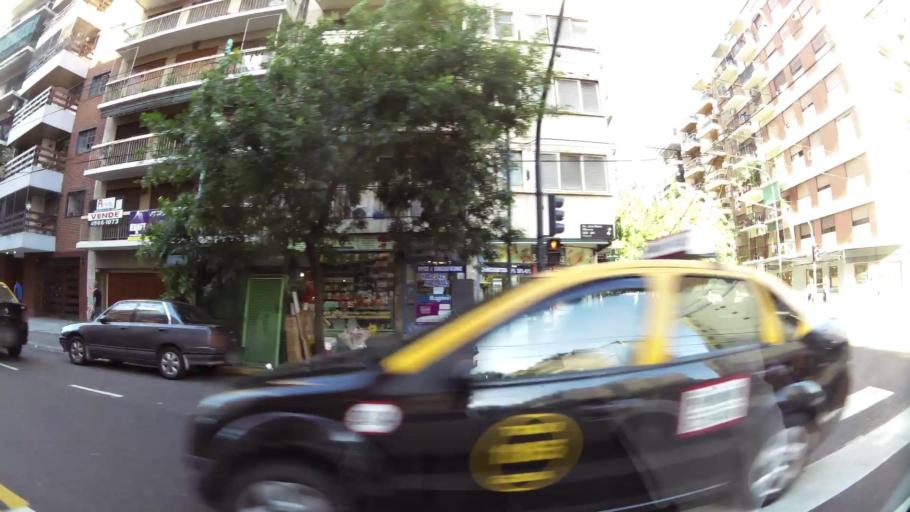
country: AR
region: Buenos Aires F.D.
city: Villa Santa Rita
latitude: -34.6212
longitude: -58.4351
